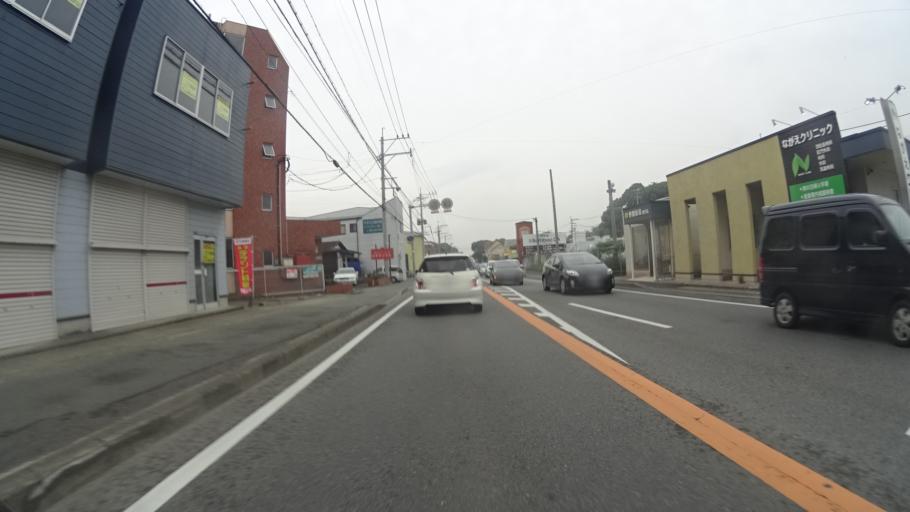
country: JP
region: Fukuoka
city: Dazaifu
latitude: 33.5193
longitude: 130.5004
